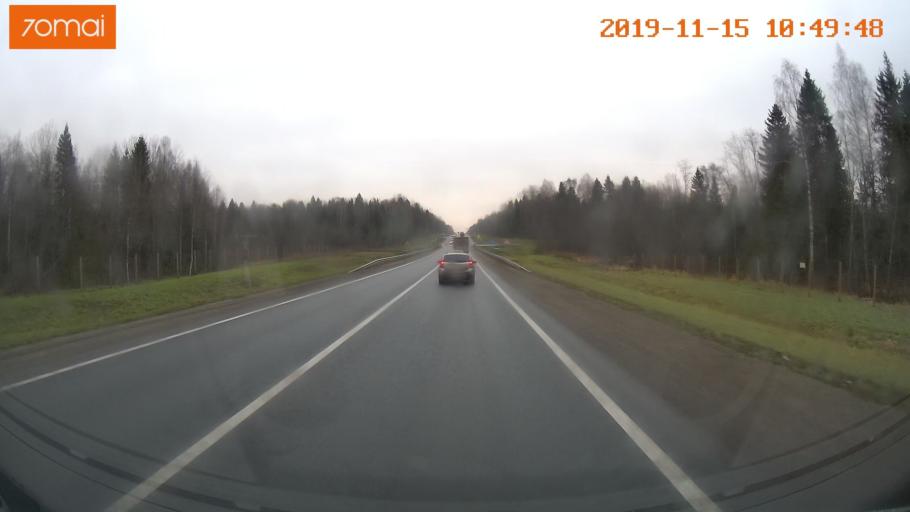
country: RU
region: Vologda
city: Sheksna
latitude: 59.1883
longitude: 38.6680
